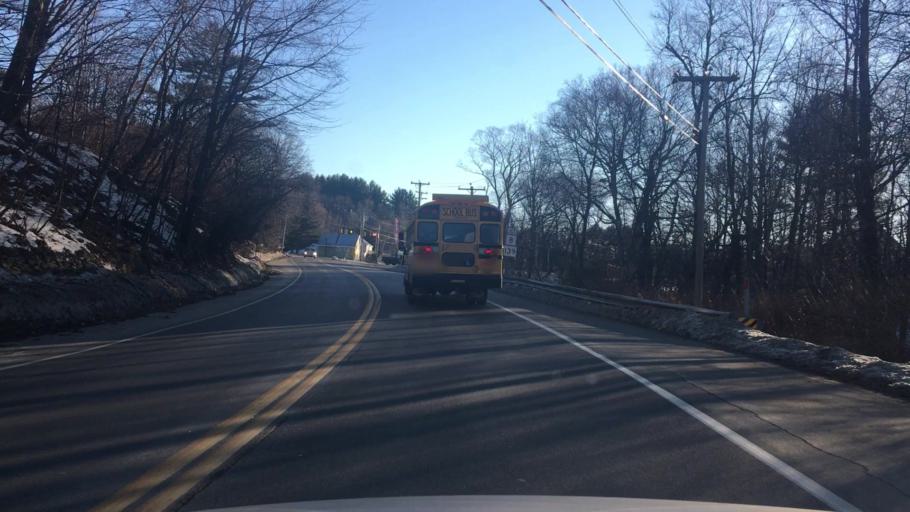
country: US
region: Maine
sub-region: Somerset County
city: Norridgewock
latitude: 44.7144
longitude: -69.7889
